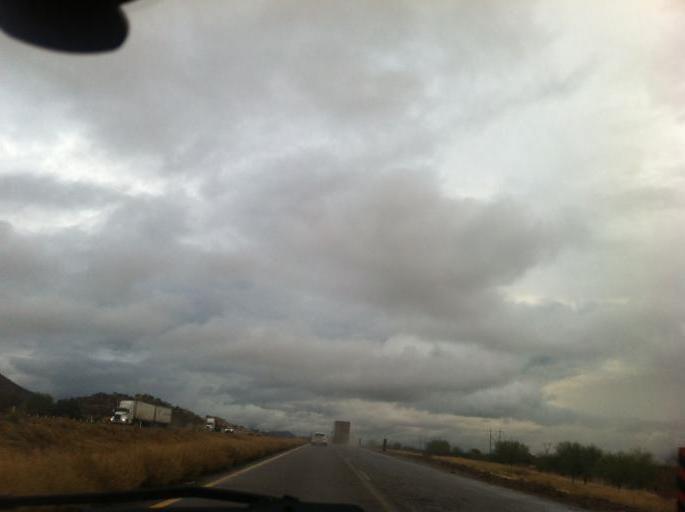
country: MX
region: Sonora
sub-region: San Miguel de Horcasitas
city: Las Mercedes [Agropecuaria]
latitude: 29.4813
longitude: -110.9976
